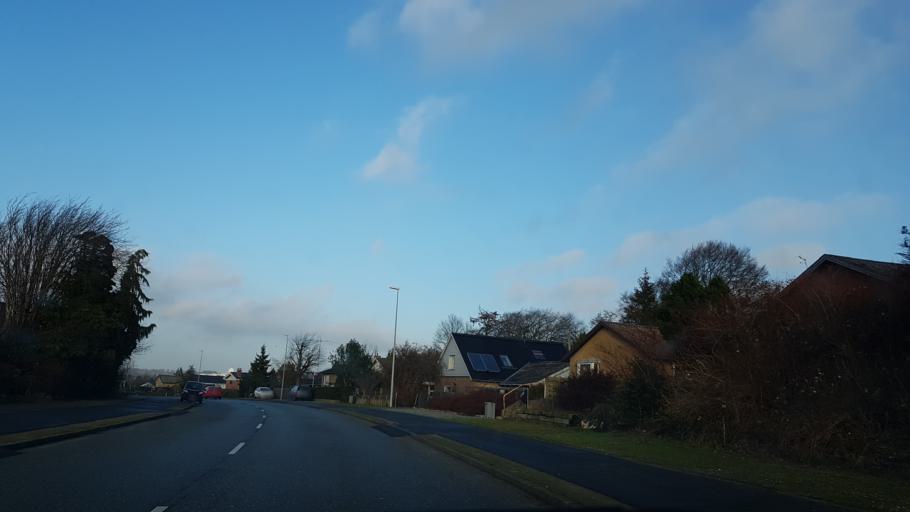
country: DK
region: South Denmark
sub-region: Haderslev Kommune
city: Haderslev
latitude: 55.2373
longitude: 9.4993
